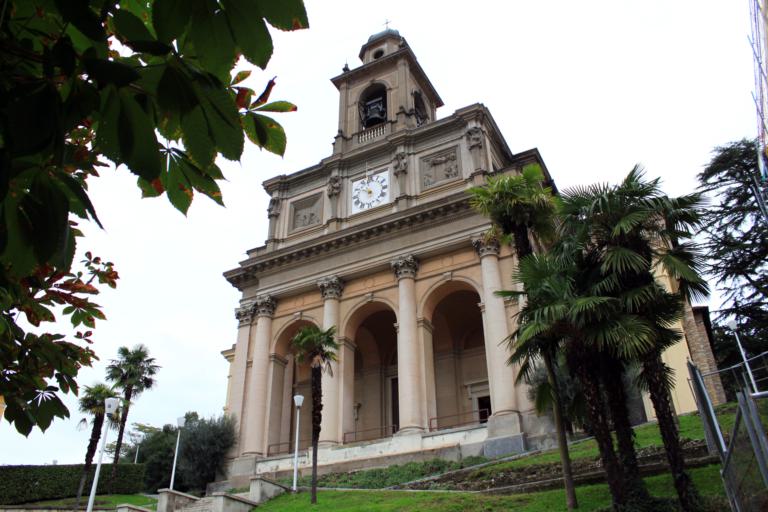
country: CH
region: Ticino
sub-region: Mendrisio District
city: Mendrisio
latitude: 45.8706
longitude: 8.9890
